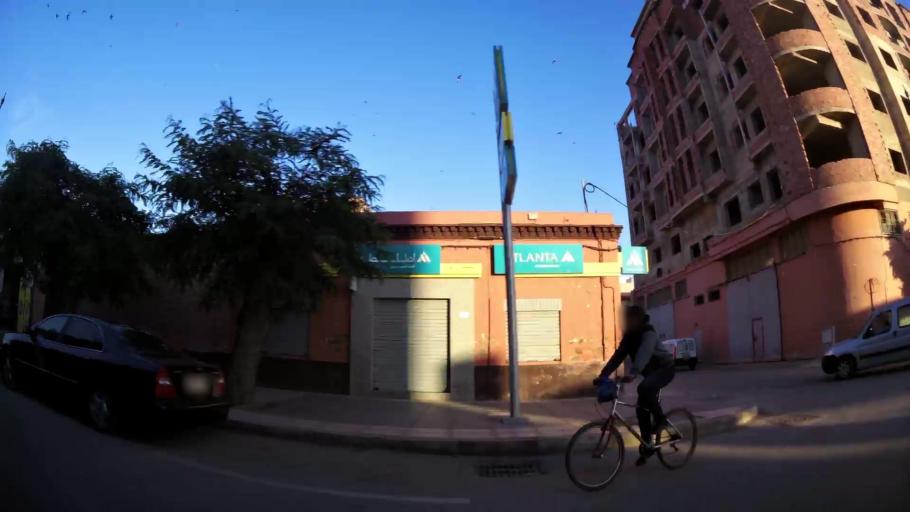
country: MA
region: Oriental
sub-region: Berkane-Taourirt
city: Berkane
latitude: 34.9245
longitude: -2.3336
